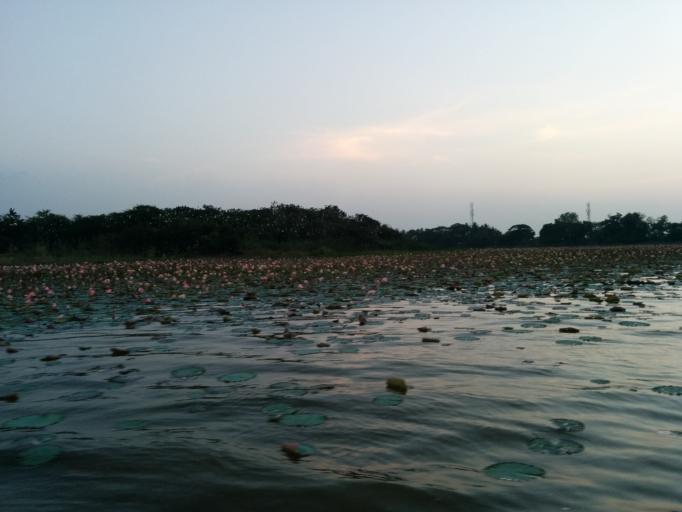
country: IN
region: Pondicherry
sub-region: Puducherry
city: Puducherry
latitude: 11.9430
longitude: 79.7505
